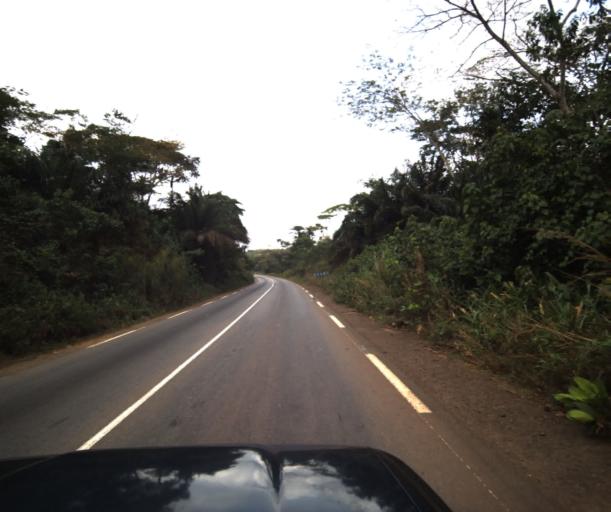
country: CM
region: Centre
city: Mbankomo
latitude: 3.7913
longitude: 11.2888
